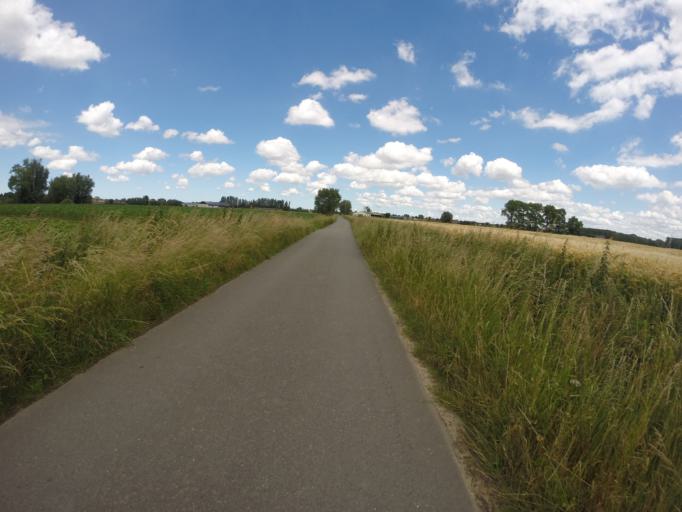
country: BE
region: Flanders
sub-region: Provincie Oost-Vlaanderen
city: Knesselare
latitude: 51.1128
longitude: 3.4234
